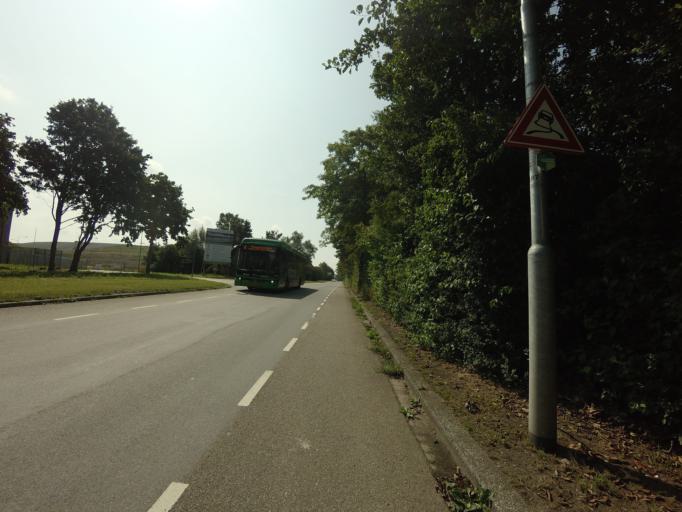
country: NL
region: South Holland
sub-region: Gemeente Sliedrecht
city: Sliedrecht
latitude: 51.8155
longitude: 4.7490
